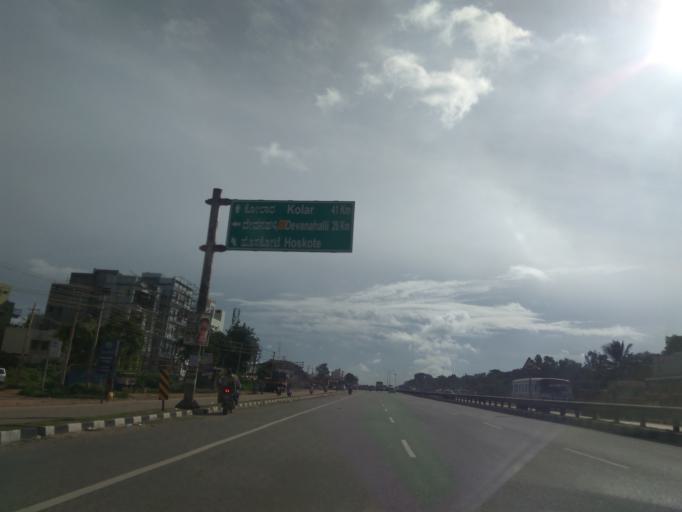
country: IN
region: Karnataka
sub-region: Bangalore Rural
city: Hoskote
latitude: 13.0689
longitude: 77.7810
